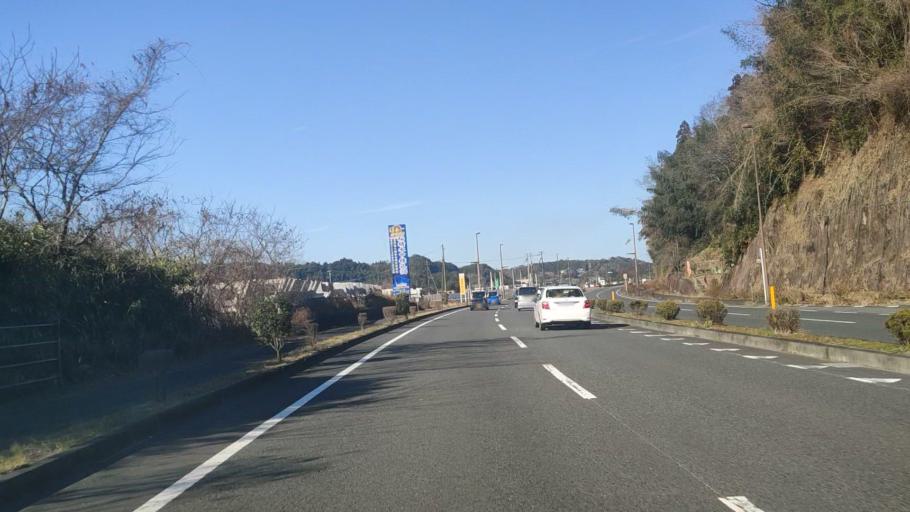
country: JP
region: Oita
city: Oita
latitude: 33.1163
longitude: 131.6539
